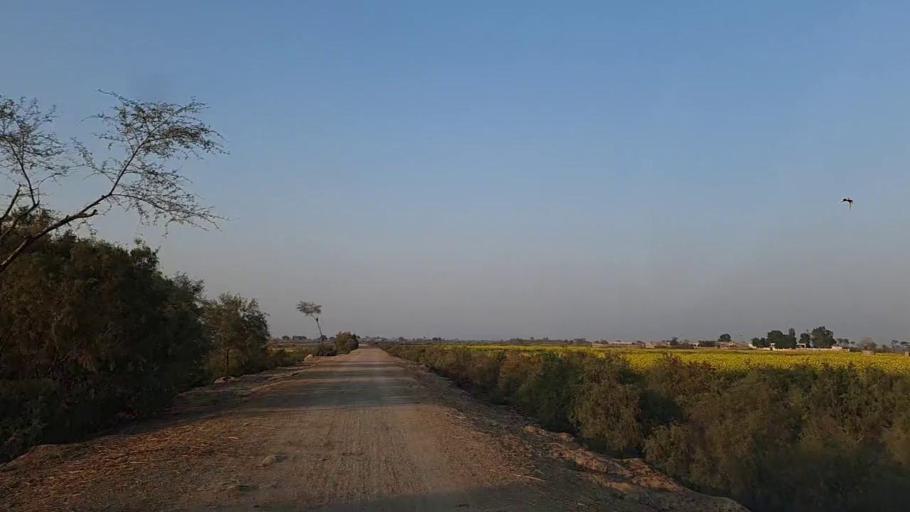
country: PK
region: Sindh
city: Bandhi
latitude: 26.5450
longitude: 68.3166
